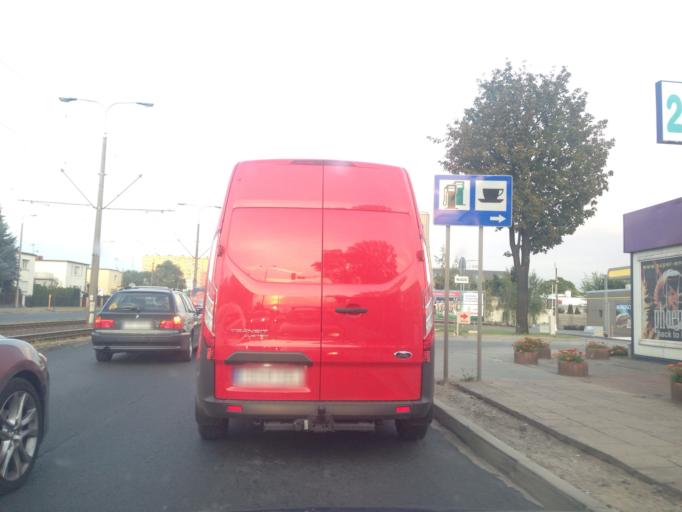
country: PL
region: Kujawsko-Pomorskie
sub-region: Bydgoszcz
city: Bydgoszcz
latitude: 53.1206
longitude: 18.0440
